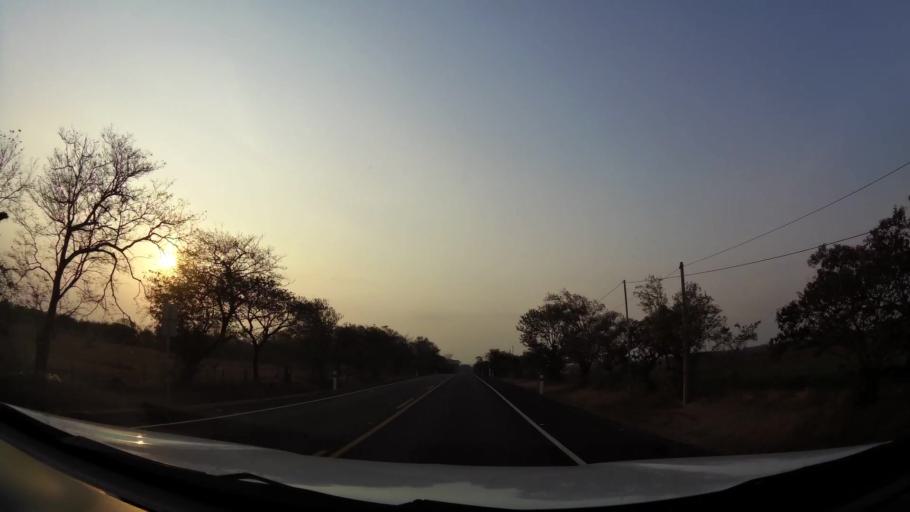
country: NI
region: Leon
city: Nagarote
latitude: 12.3095
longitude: -86.6035
